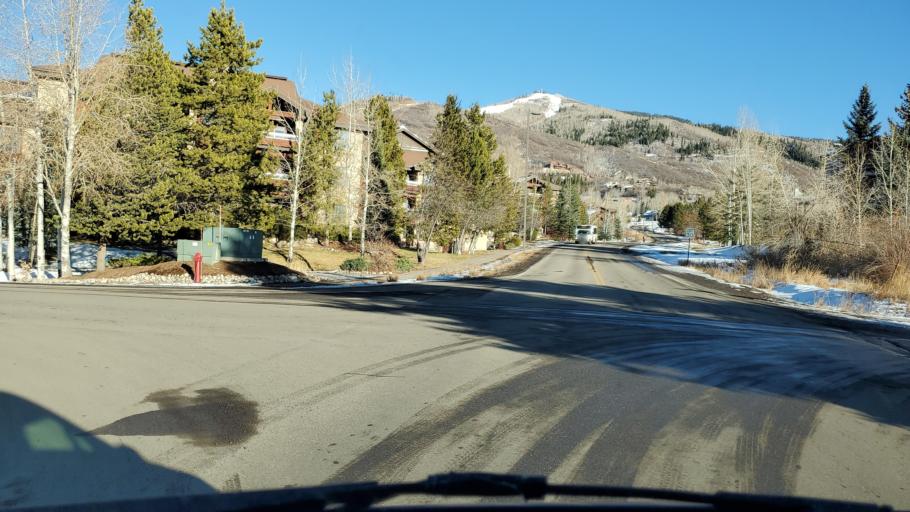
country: US
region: Colorado
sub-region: Routt County
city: Steamboat Springs
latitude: 40.4512
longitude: -106.8056
